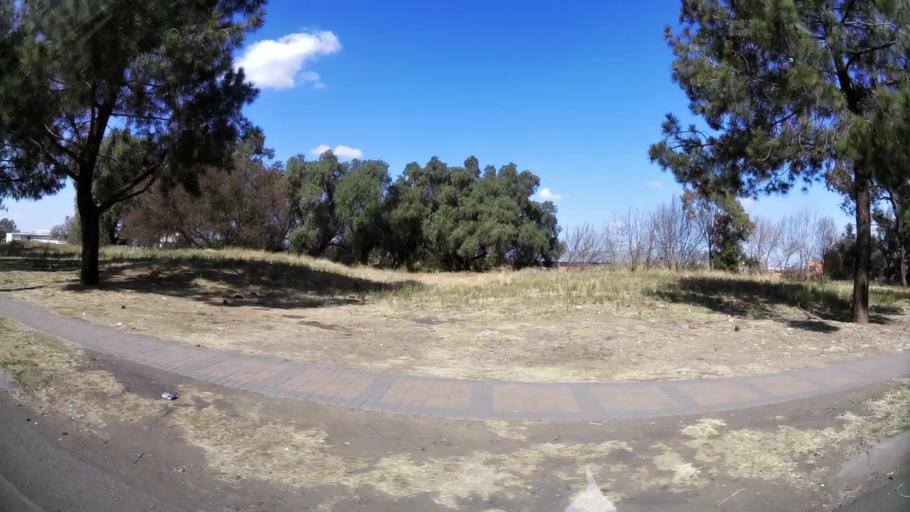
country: ZA
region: Orange Free State
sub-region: Mangaung Metropolitan Municipality
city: Bloemfontein
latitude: -29.1188
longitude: 26.2337
